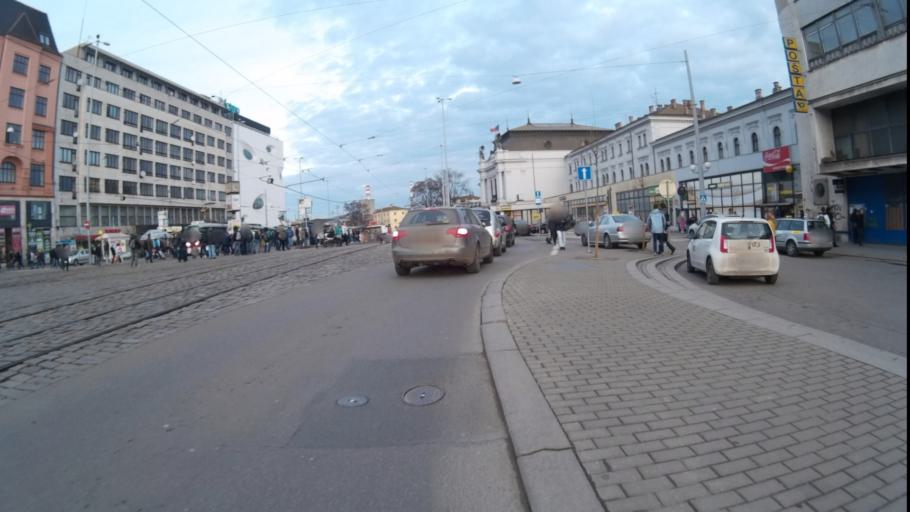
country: CZ
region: South Moravian
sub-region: Mesto Brno
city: Brno
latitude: 49.1910
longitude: 16.6120
